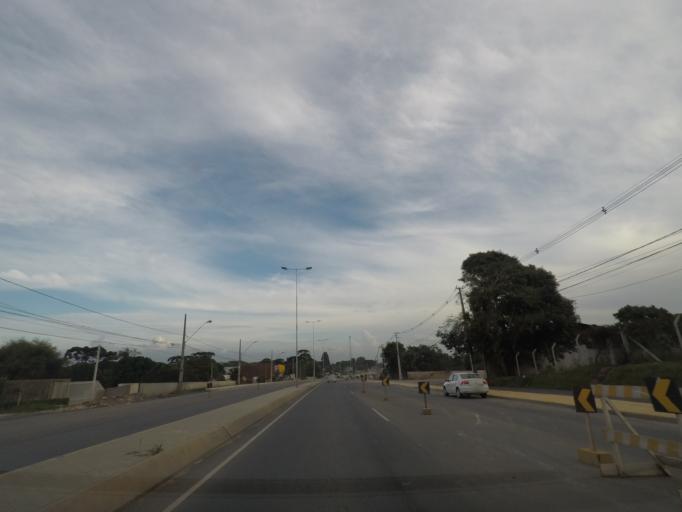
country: BR
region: Parana
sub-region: Colombo
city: Colombo
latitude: -25.3205
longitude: -49.2199
